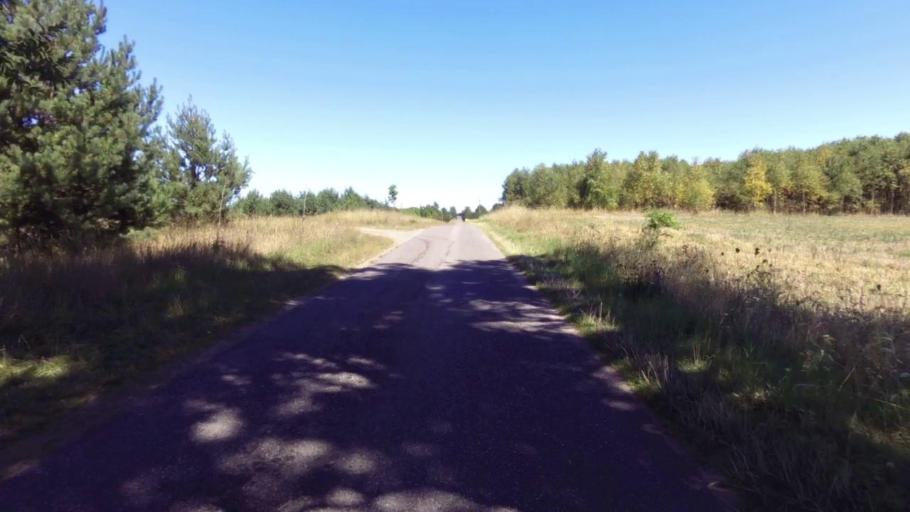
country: PL
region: West Pomeranian Voivodeship
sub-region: Powiat szczecinecki
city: Lubowo
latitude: 53.5805
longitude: 16.3769
